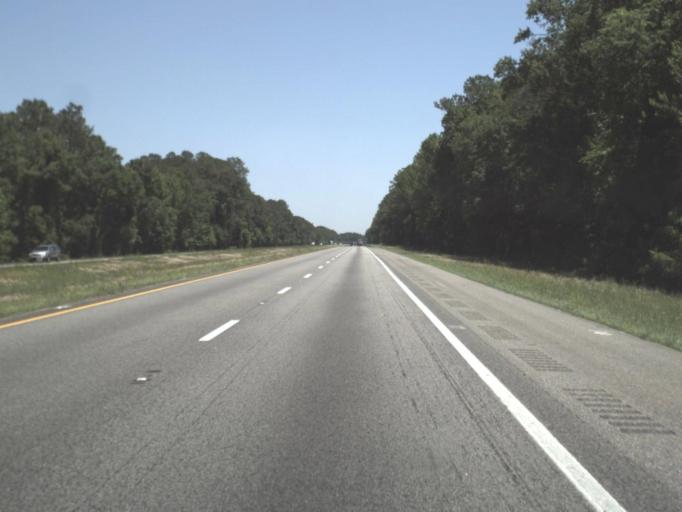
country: US
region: Florida
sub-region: Jefferson County
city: Monticello
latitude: 30.4727
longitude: -83.8450
